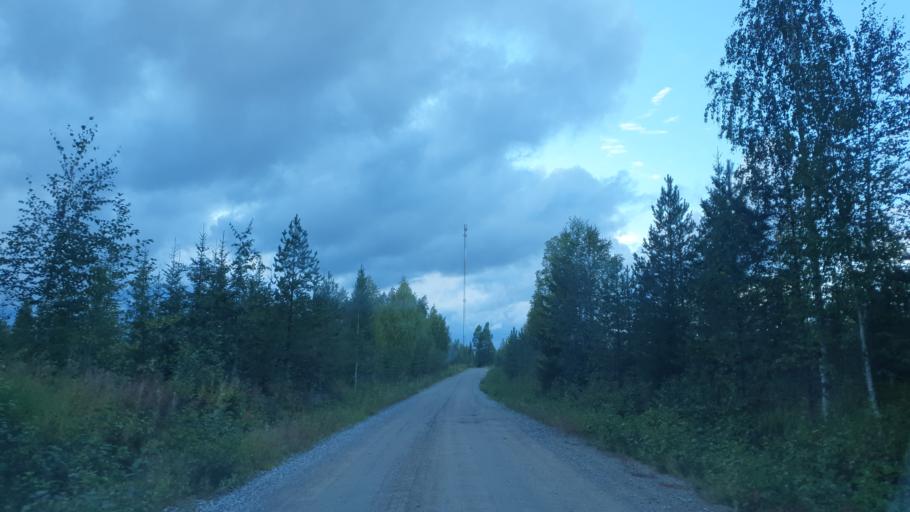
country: FI
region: Kainuu
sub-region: Kehys-Kainuu
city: Kuhmo
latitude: 64.3392
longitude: 29.8890
